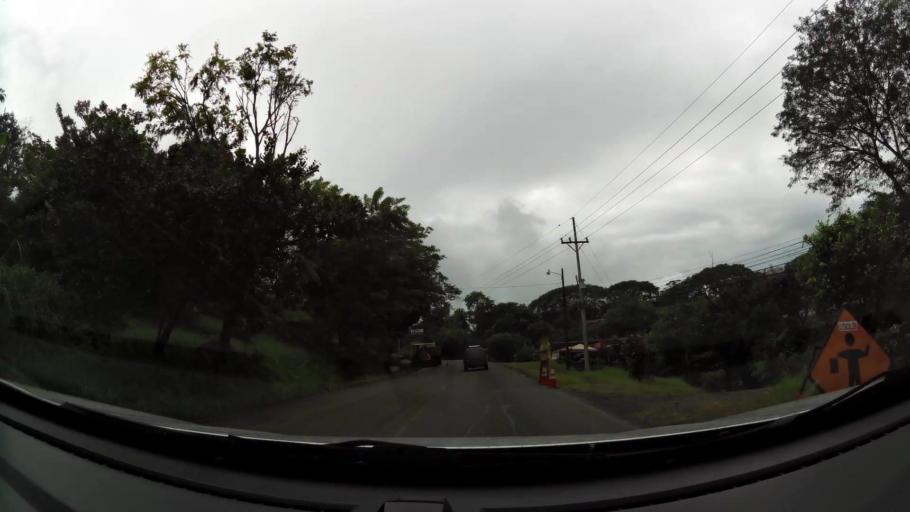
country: CR
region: Puntarenas
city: Esparza
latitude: 10.0001
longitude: -84.6755
